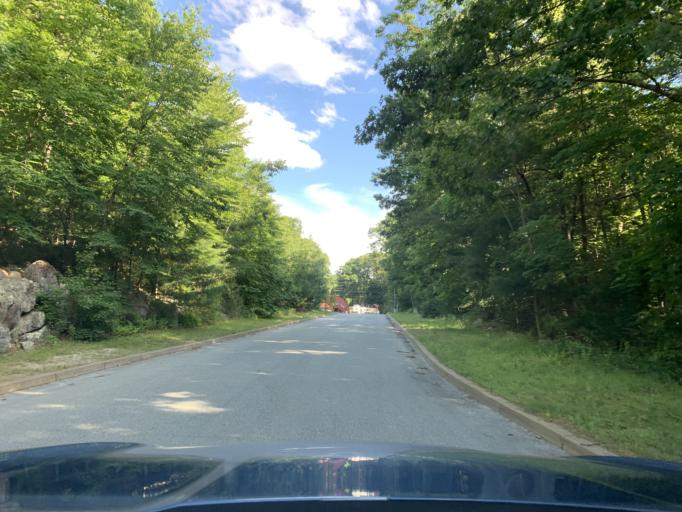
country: US
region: Rhode Island
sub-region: Kent County
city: West Warwick
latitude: 41.6599
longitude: -71.5238
